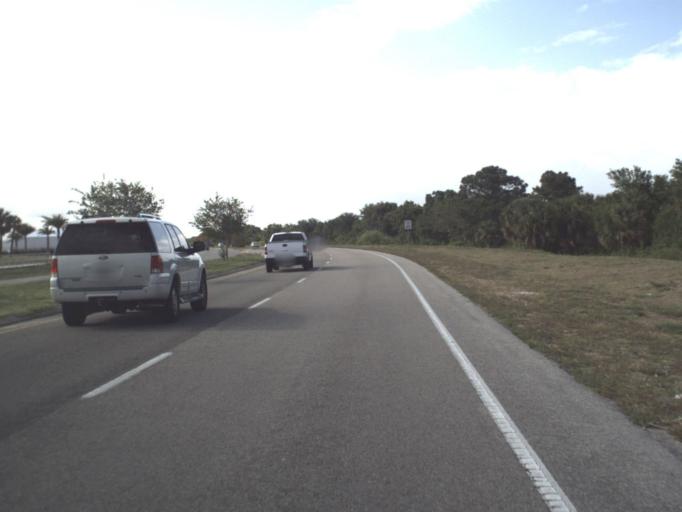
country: US
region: Florida
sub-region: Brevard County
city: Melbourne
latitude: 28.1007
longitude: -80.6232
